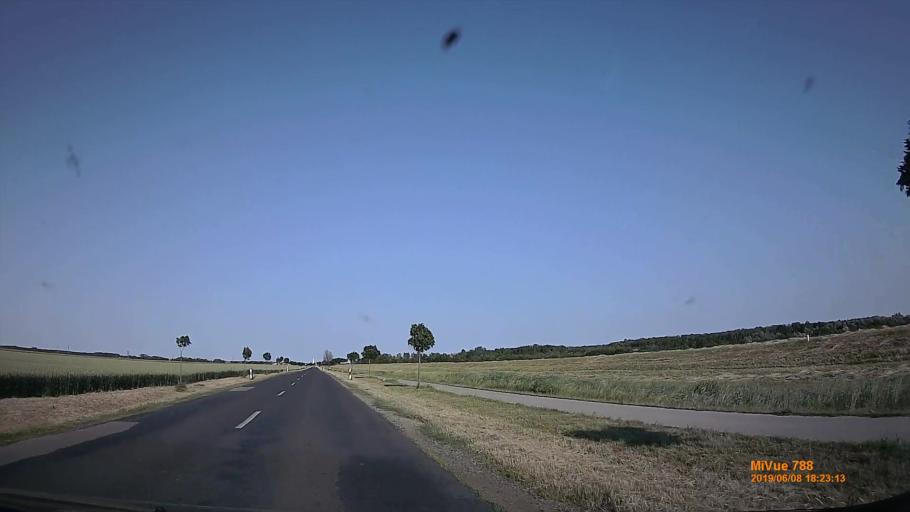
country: HU
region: Vas
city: Buk
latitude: 47.3715
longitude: 16.7829
